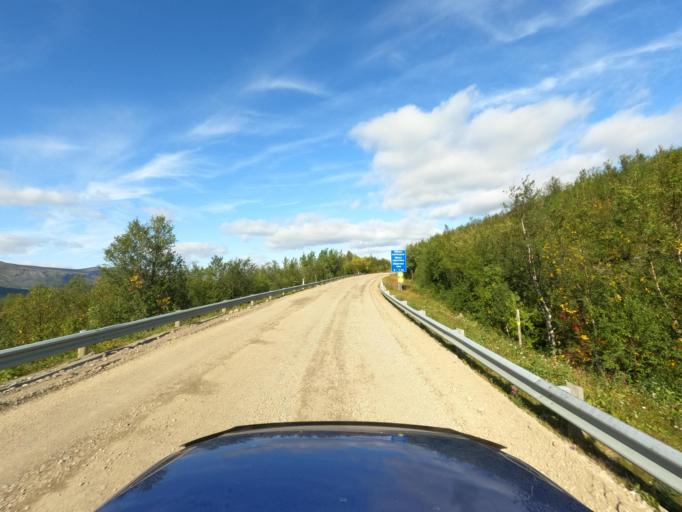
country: NO
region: Finnmark Fylke
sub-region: Porsanger
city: Lakselv
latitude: 69.8807
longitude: 25.0220
